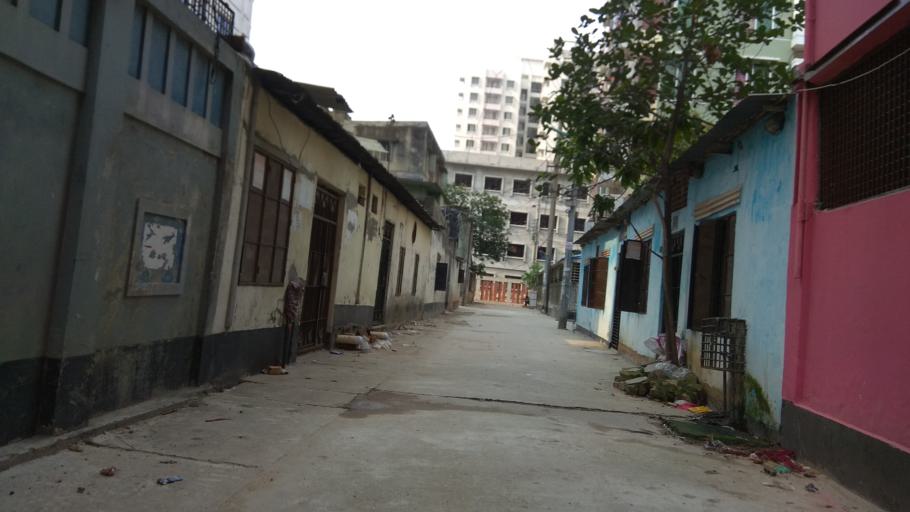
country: BD
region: Dhaka
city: Tungi
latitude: 23.8149
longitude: 90.3614
